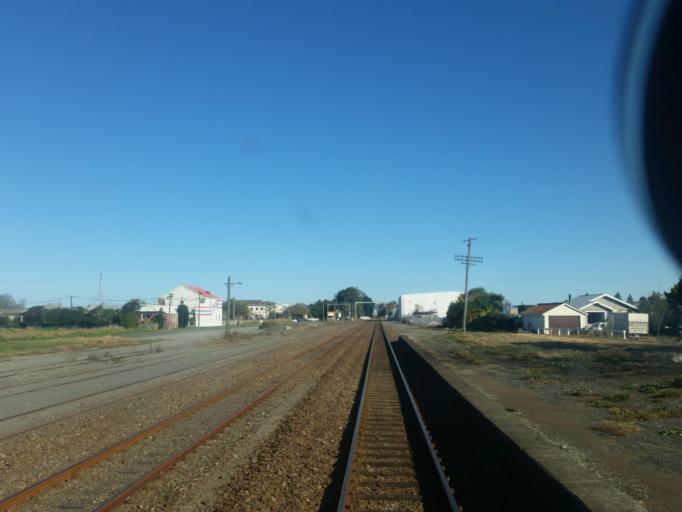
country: NZ
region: Canterbury
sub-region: Waimakariri District
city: Kaiapoi
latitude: -43.4480
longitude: 172.6374
